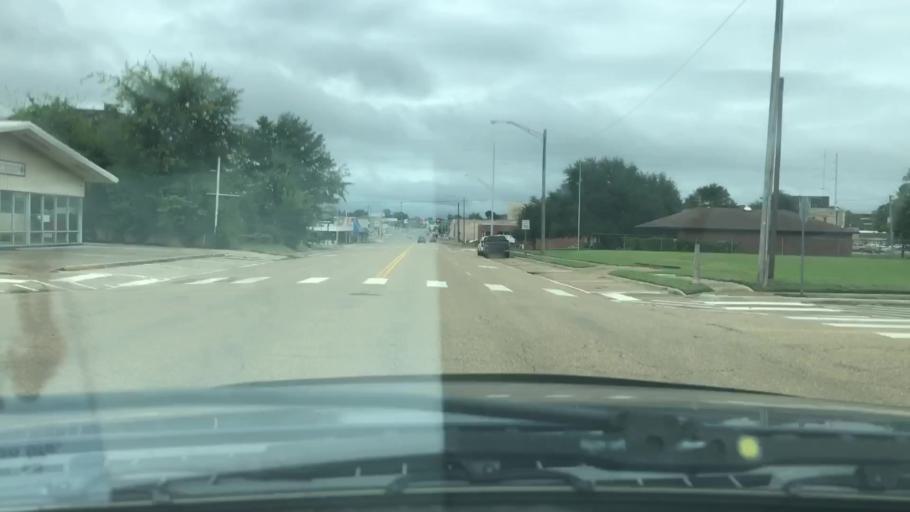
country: US
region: Texas
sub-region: Bowie County
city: Texarkana
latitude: 33.4232
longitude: -94.0468
